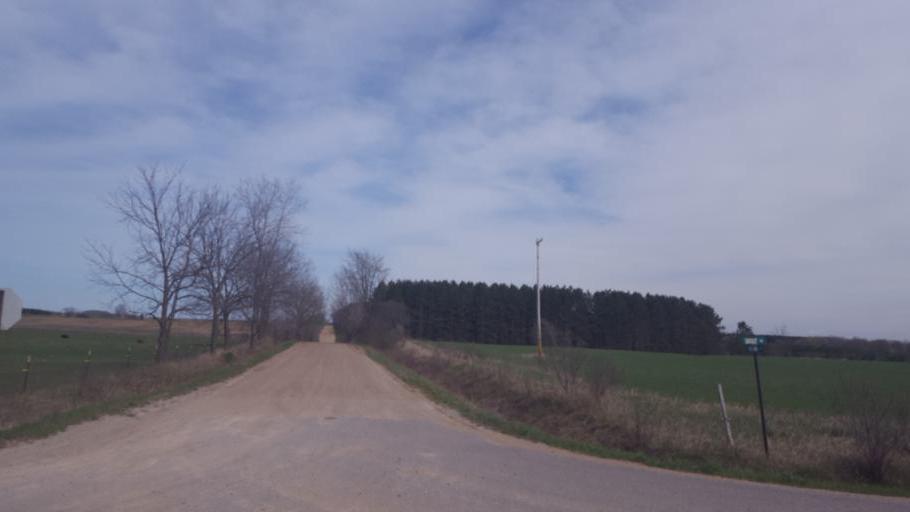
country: US
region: Michigan
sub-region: Gladwin County
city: Gladwin
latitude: 43.9524
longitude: -84.5451
